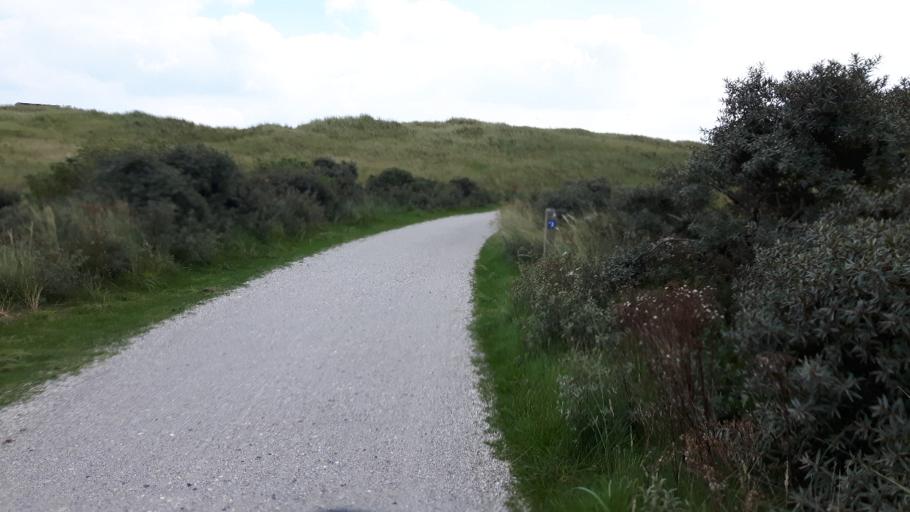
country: NL
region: Friesland
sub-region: Gemeente Dongeradeel
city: Holwerd
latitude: 53.4599
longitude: 5.9014
